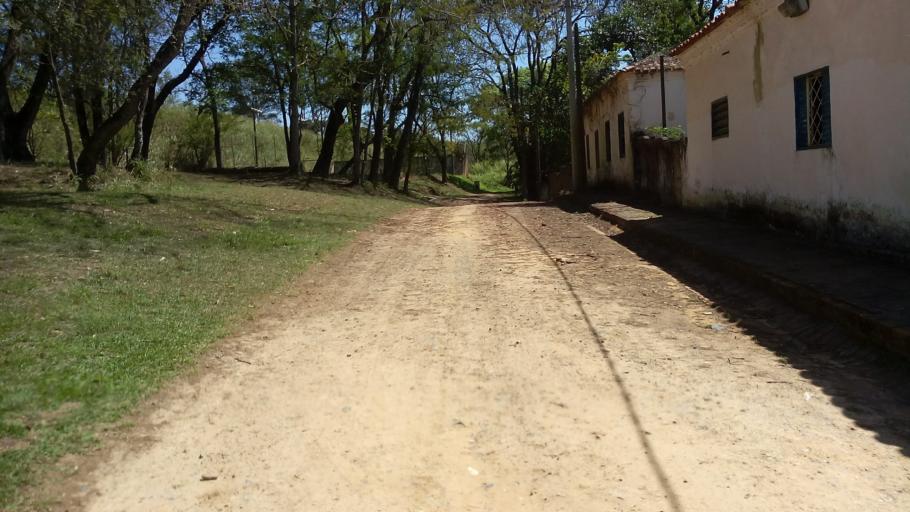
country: BR
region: Sao Paulo
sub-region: Aracoiaba Da Serra
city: Aracoiaba da Serra
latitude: -23.4267
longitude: -47.5996
